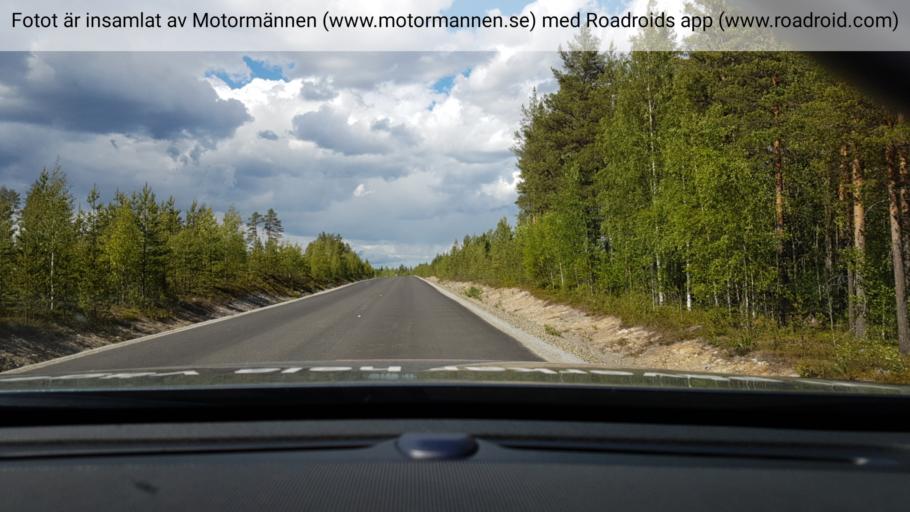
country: SE
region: Vaesterbotten
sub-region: Lycksele Kommun
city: Lycksele
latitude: 63.9817
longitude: 18.4862
